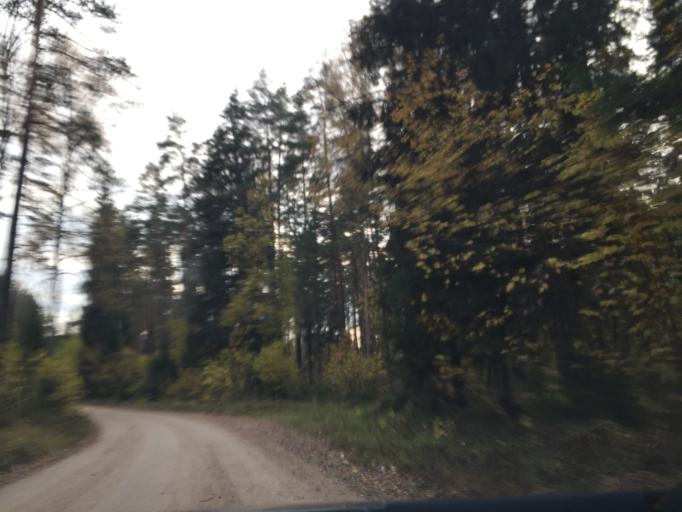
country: LV
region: Cesu Rajons
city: Cesis
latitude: 57.3498
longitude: 25.1631
